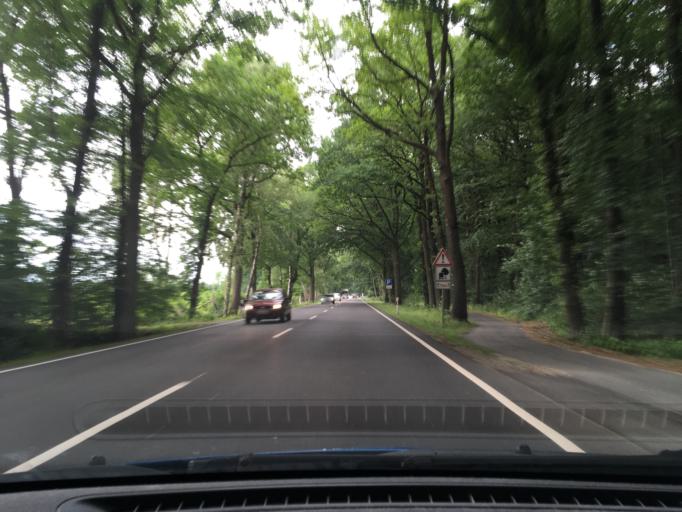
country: DE
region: Lower Saxony
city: Wenzendorf
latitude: 53.3542
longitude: 9.8083
